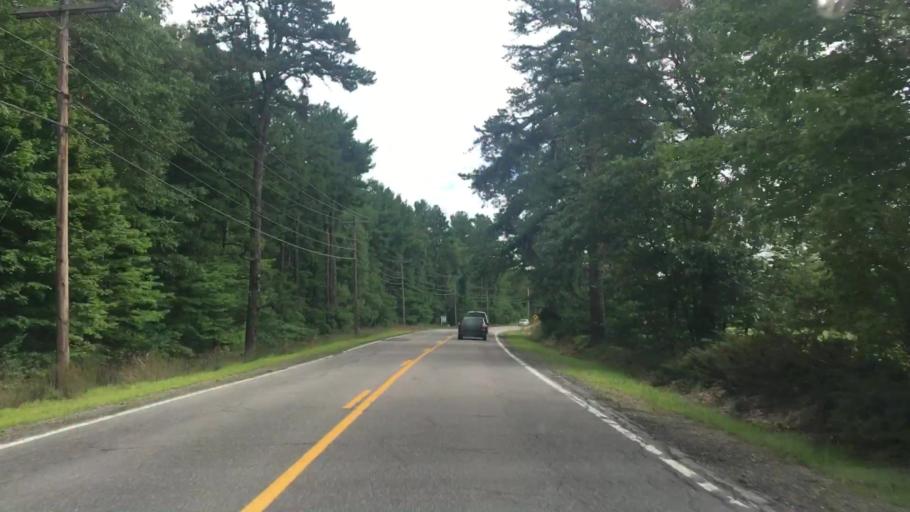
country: US
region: Maine
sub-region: York County
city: Lake Arrowhead
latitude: 43.6101
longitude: -70.7164
